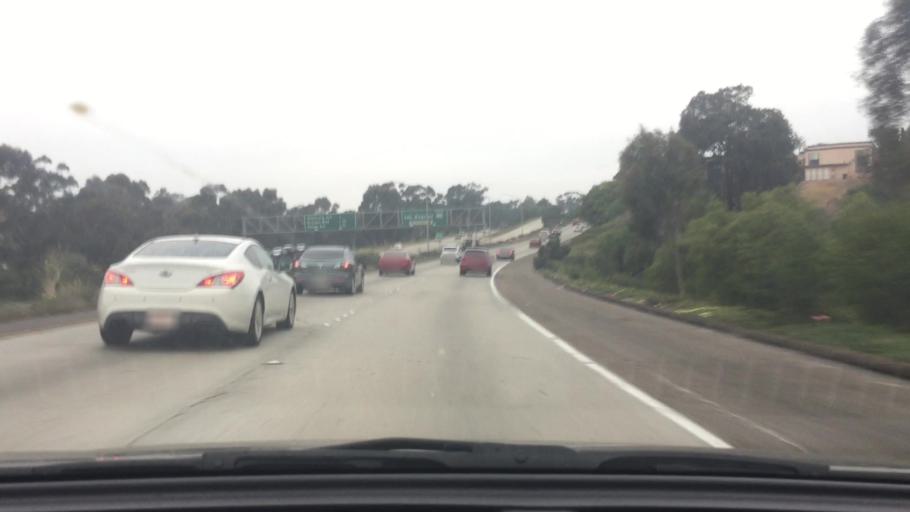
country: US
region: California
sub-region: San Diego County
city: San Diego
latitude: 32.7330
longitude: -117.1111
